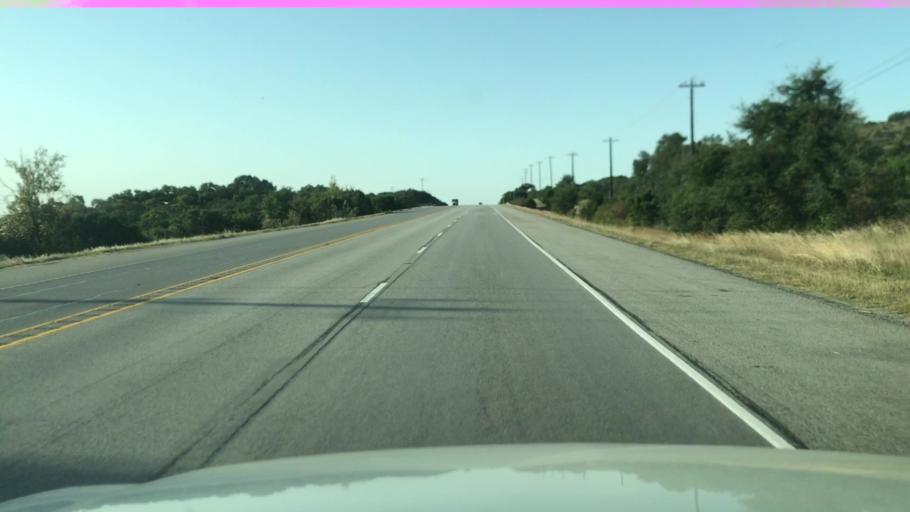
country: US
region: Texas
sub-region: Blanco County
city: Blanco
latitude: 30.1752
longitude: -98.3804
